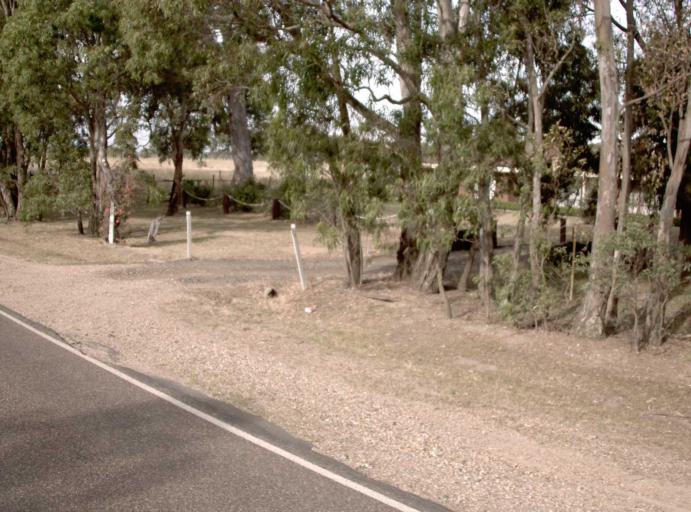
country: AU
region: Victoria
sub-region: Wellington
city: Heyfield
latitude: -38.0298
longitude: 146.6680
